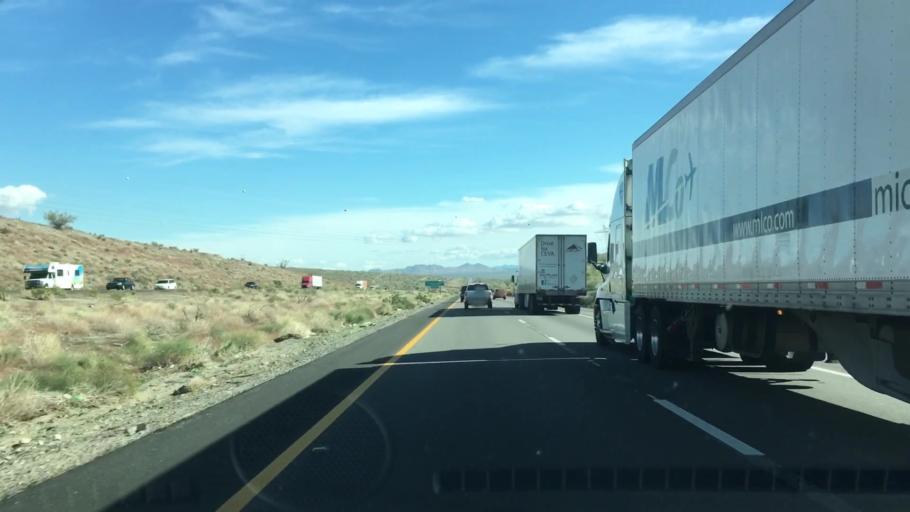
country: US
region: California
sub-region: Riverside County
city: Mecca
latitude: 33.6717
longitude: -115.9261
